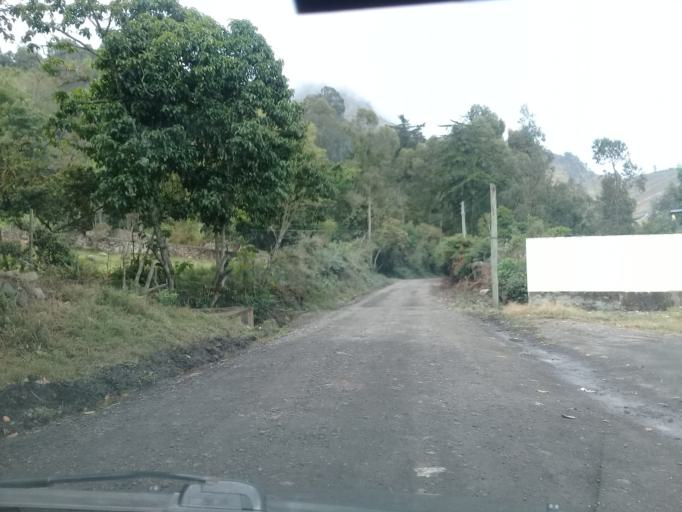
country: CO
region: Cundinamarca
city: Une
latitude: 4.4040
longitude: -73.9905
